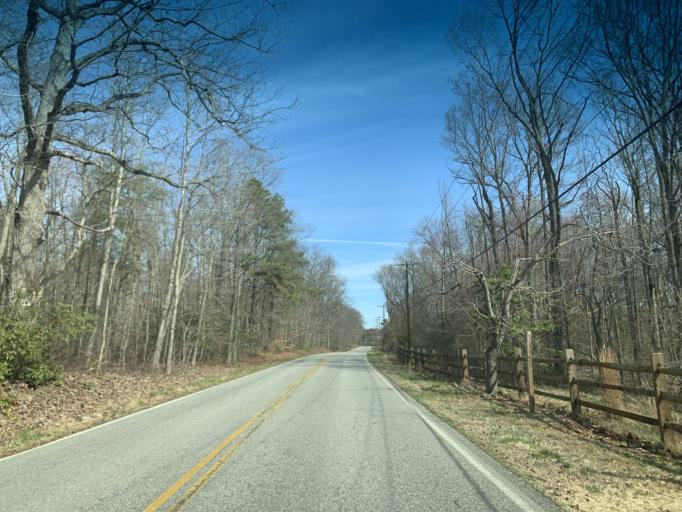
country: US
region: Maryland
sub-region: Cecil County
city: Charlestown
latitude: 39.5716
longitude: -75.9886
